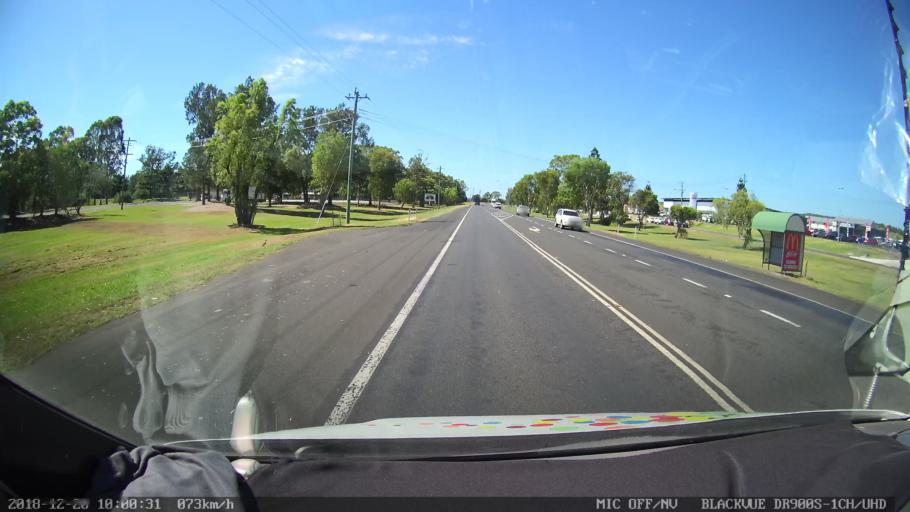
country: AU
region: New South Wales
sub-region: Lismore Municipality
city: Lismore
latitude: -28.8334
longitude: 153.2647
